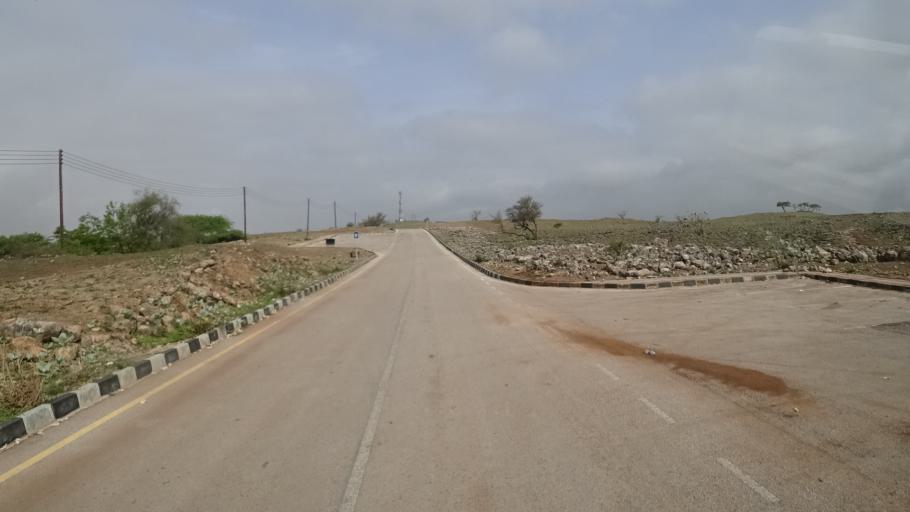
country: OM
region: Zufar
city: Salalah
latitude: 17.0773
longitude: 54.4499
